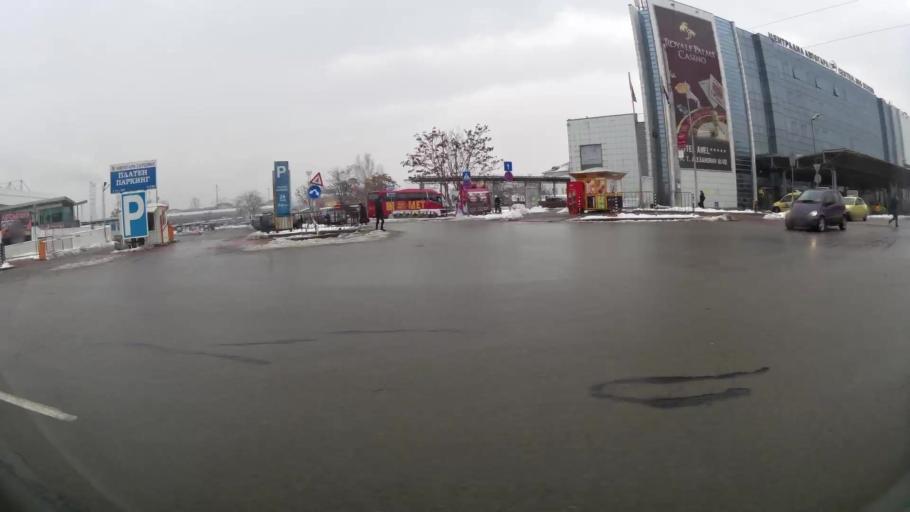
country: BG
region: Sofia-Capital
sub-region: Stolichna Obshtina
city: Sofia
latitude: 42.7103
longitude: 23.3223
